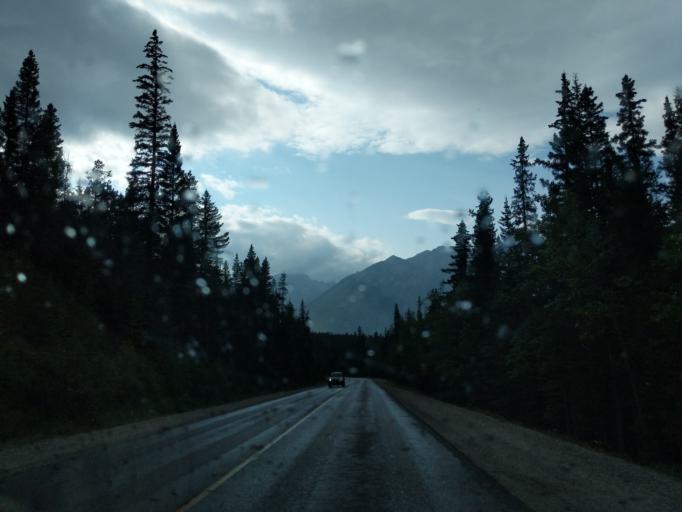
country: CA
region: Alberta
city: Banff
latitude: 51.1633
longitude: -115.5749
